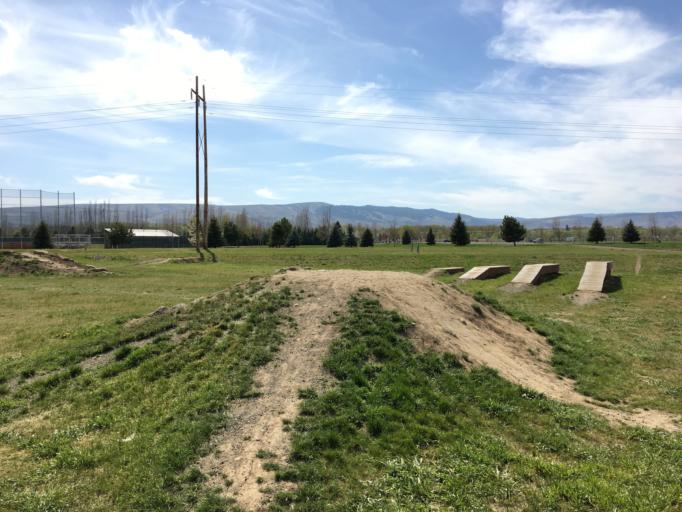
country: US
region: Washington
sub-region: Kittitas County
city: Ellensburg
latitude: 46.9940
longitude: -120.5620
